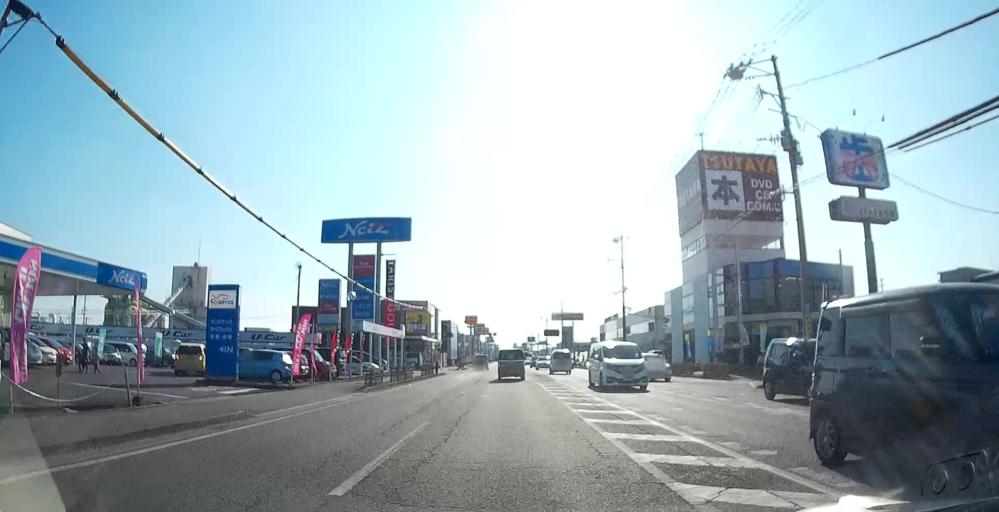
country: JP
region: Kumamoto
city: Kumamoto
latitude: 32.7597
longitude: 130.6888
